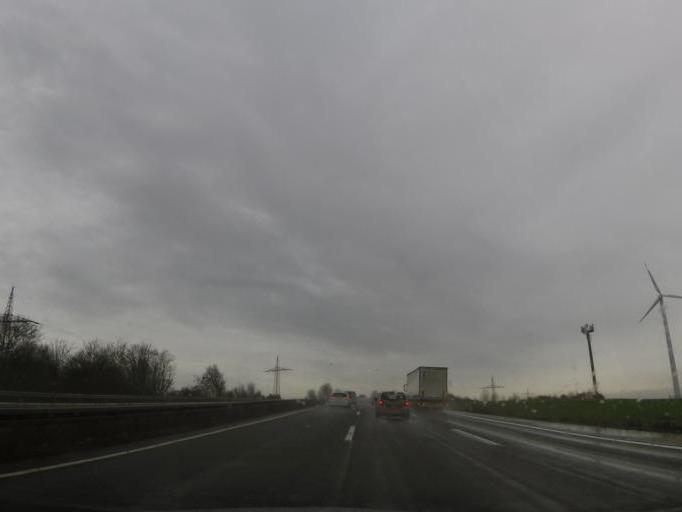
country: DE
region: Hesse
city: Bad Camberg
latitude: 50.2768
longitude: 8.2429
